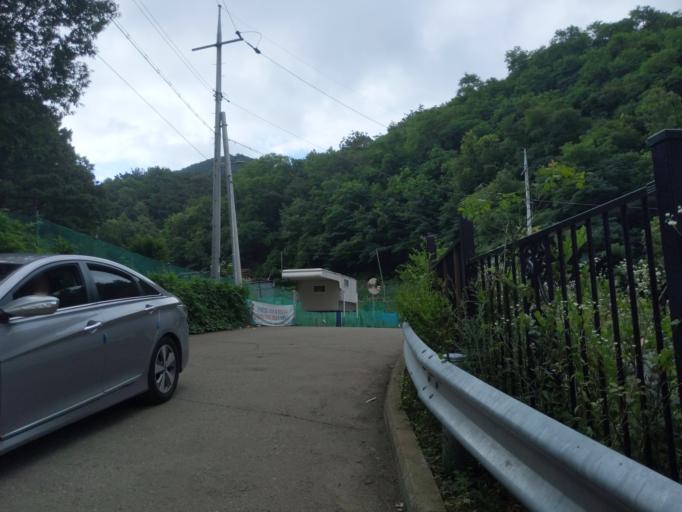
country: KR
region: Daegu
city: Hwawon
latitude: 35.7982
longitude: 128.5327
